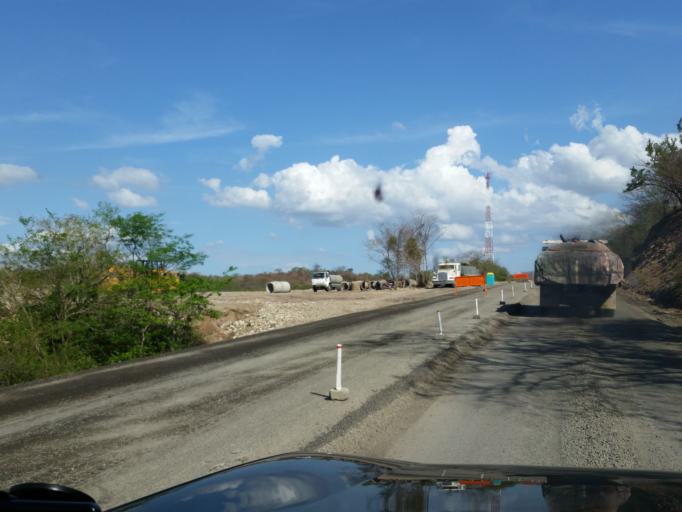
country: NI
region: Leon
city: Nagarote
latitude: 12.1745
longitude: -86.6666
